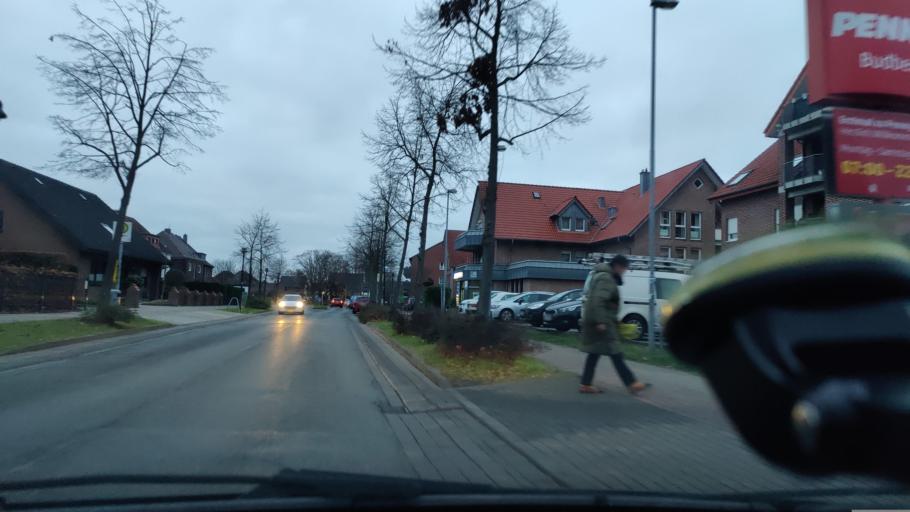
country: DE
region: North Rhine-Westphalia
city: Rheinberg
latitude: 51.5337
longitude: 6.6384
